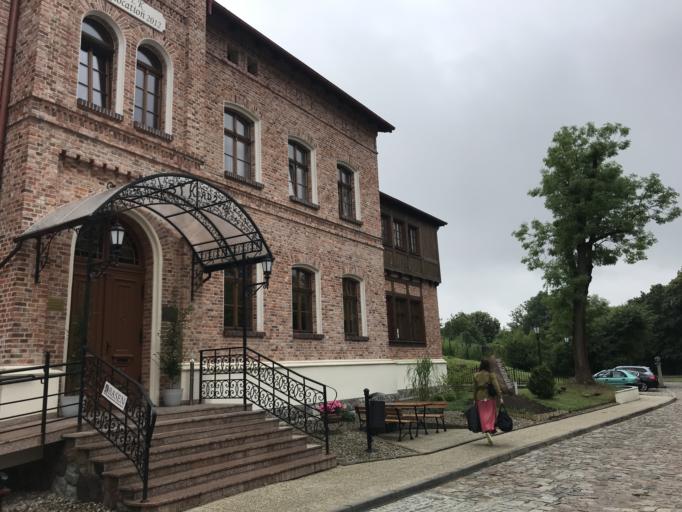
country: PL
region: Warmian-Masurian Voivodeship
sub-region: Powiat elblaski
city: Elblag
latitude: 54.1732
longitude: 19.4251
